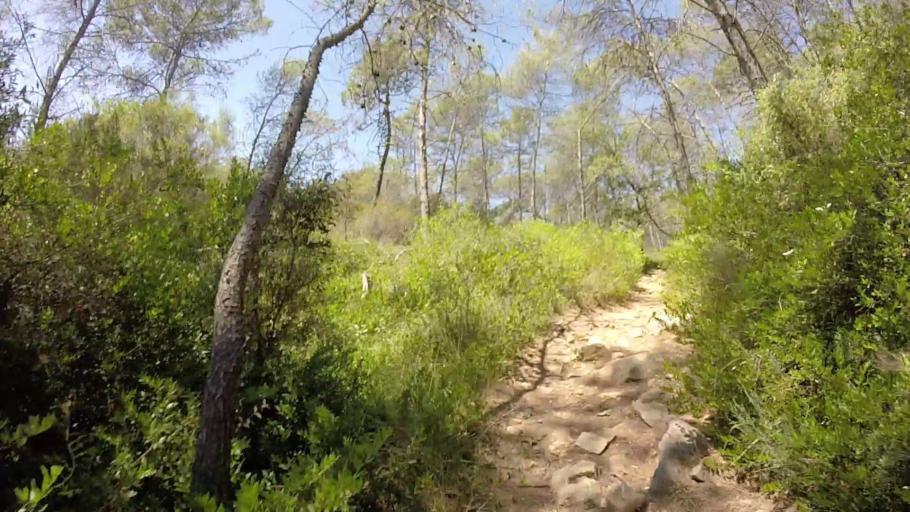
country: FR
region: Provence-Alpes-Cote d'Azur
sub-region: Departement des Alpes-Maritimes
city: Vallauris
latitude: 43.6075
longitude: 7.0490
